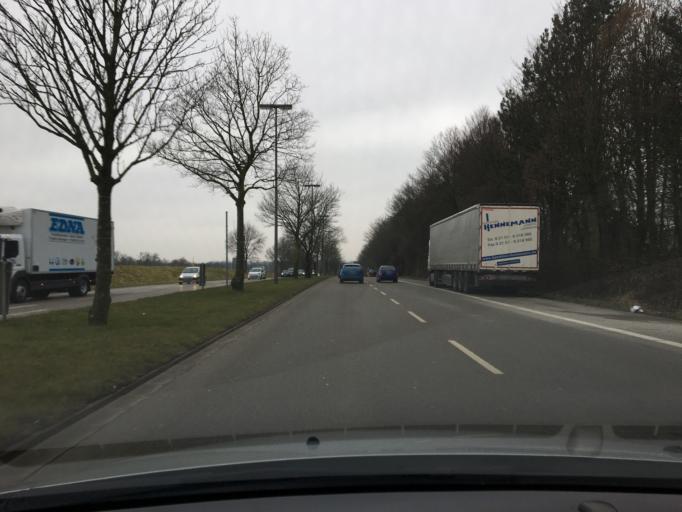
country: DE
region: North Rhine-Westphalia
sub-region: Regierungsbezirk Munster
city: Gelsenkirchen
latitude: 51.4584
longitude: 7.1363
